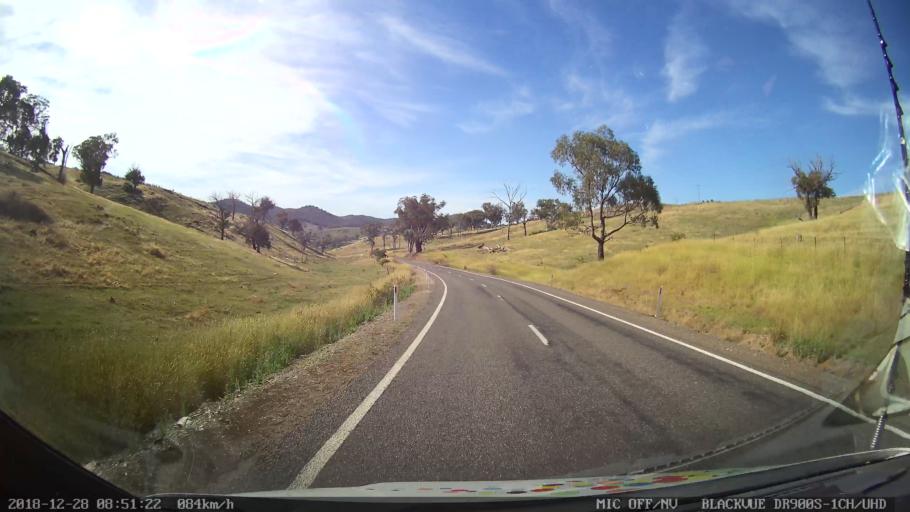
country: AU
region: New South Wales
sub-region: Upper Lachlan Shire
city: Crookwell
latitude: -34.0674
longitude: 149.3396
